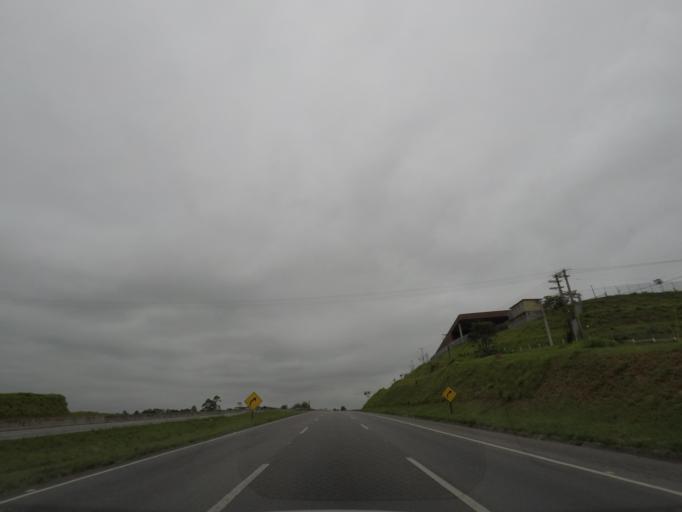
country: BR
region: Sao Paulo
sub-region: Jacarei
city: Jacarei
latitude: -23.2676
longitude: -46.0612
